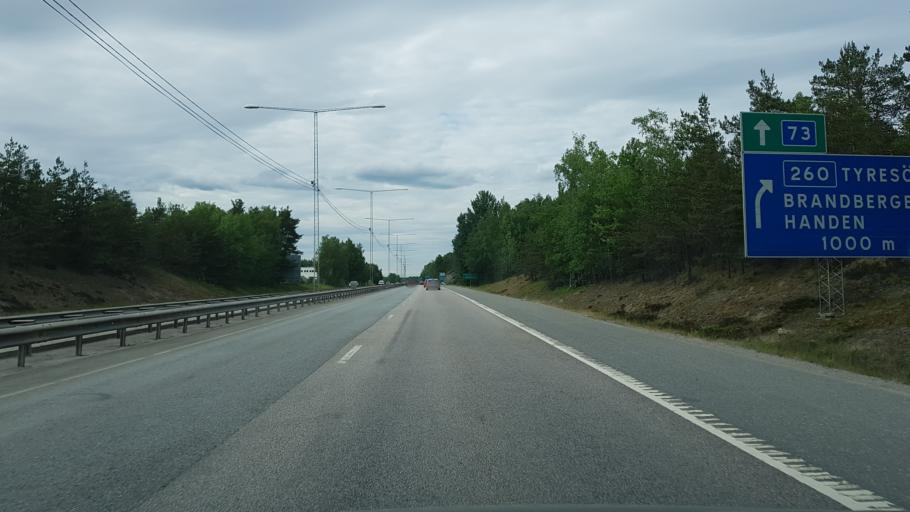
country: SE
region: Stockholm
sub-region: Haninge Kommun
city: Haninge
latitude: 59.1678
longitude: 18.1593
